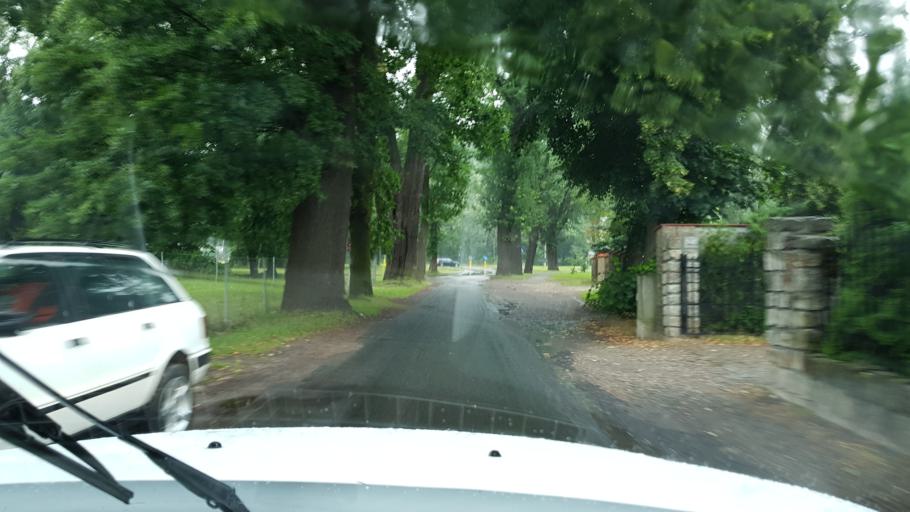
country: PL
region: West Pomeranian Voivodeship
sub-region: Powiat gryfinski
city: Chojna
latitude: 52.9601
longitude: 14.4248
